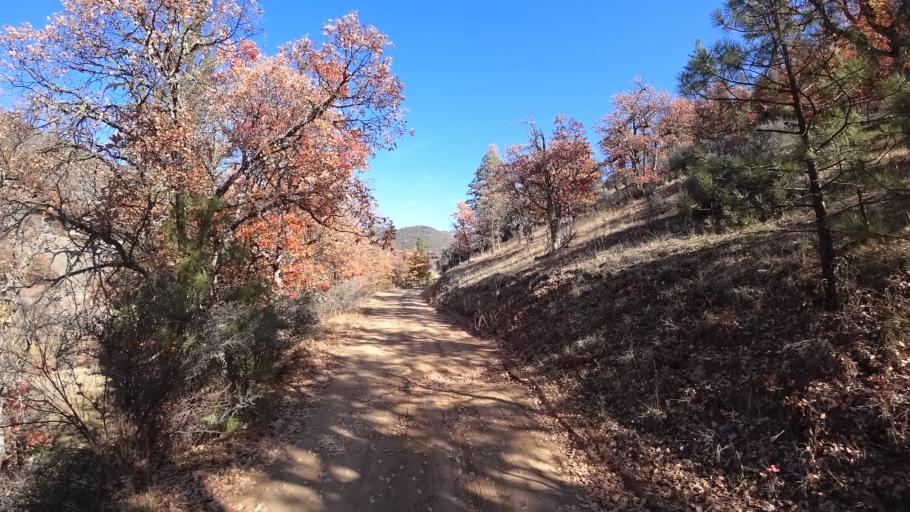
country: US
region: California
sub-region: Siskiyou County
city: Yreka
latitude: 41.8652
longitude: -122.7431
